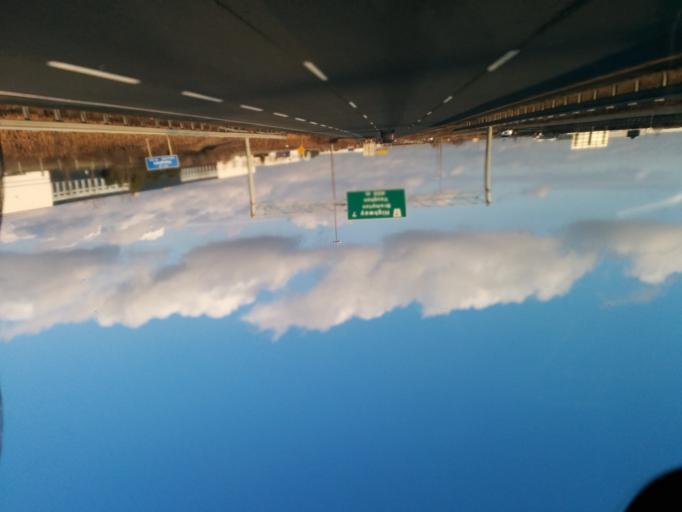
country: CA
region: Ontario
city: Etobicoke
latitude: 43.7618
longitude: -79.6328
